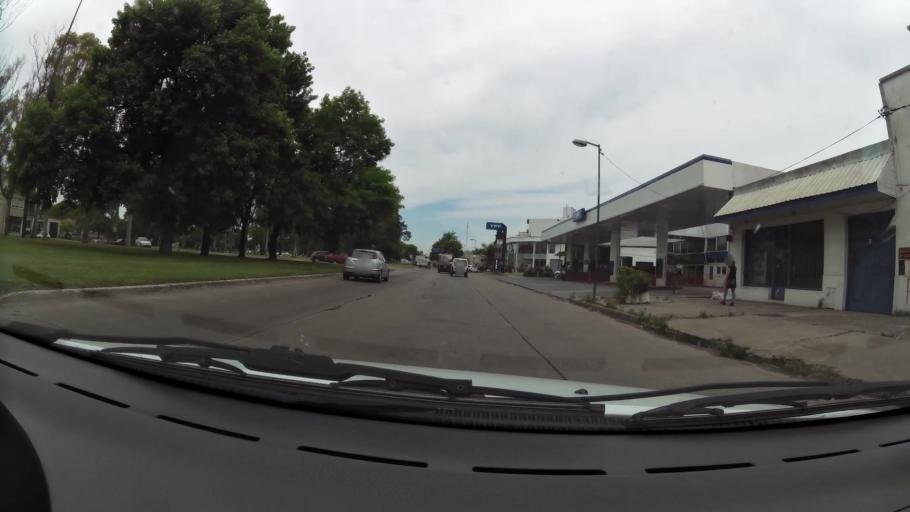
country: AR
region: Buenos Aires
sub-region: Partido de La Plata
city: La Plata
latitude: -34.9211
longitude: -57.9904
